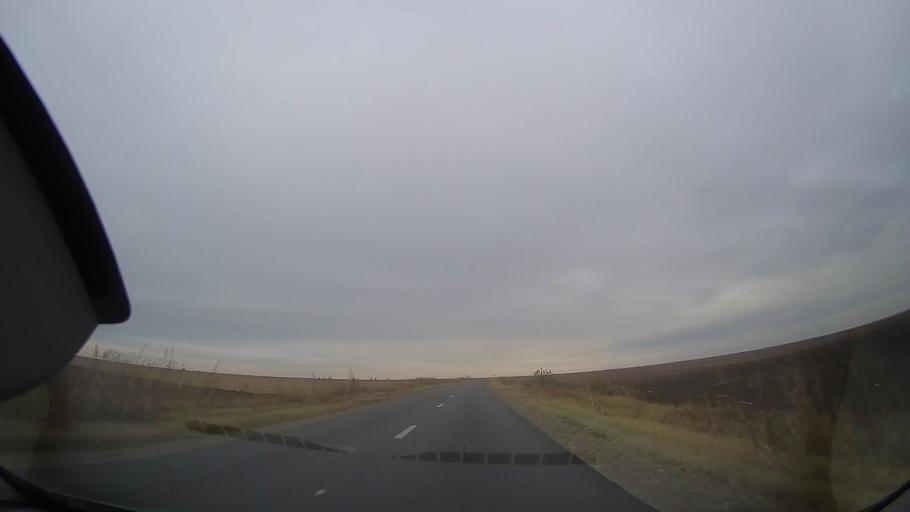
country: RO
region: Ialomita
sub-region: Oras Amara
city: Amara
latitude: 44.6443
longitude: 27.3005
